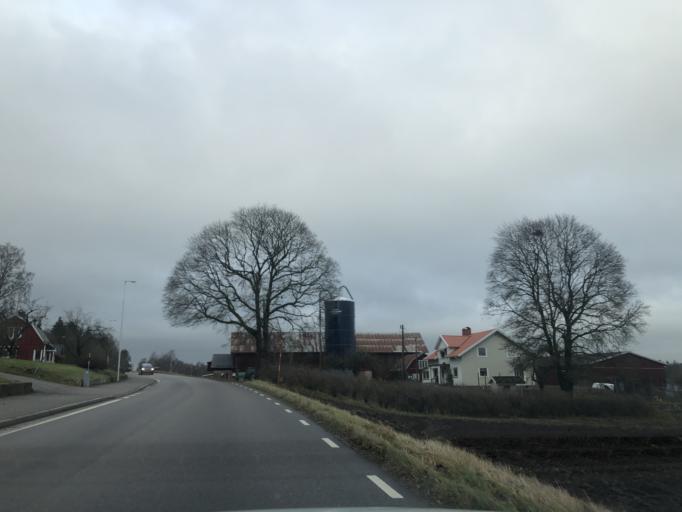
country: SE
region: Vaestra Goetaland
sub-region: Ulricehamns Kommun
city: Ulricehamn
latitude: 57.9340
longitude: 13.4866
